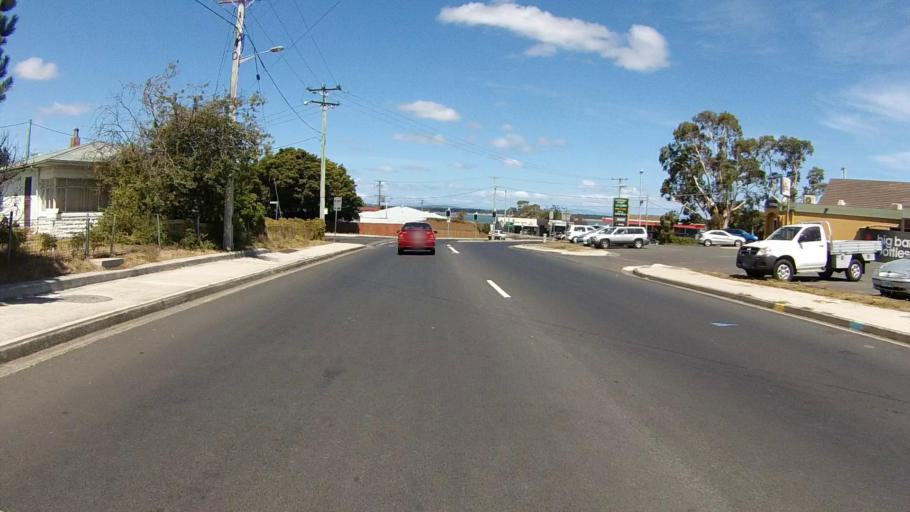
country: AU
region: Tasmania
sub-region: Sorell
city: Sorell
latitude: -42.8030
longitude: 147.5320
